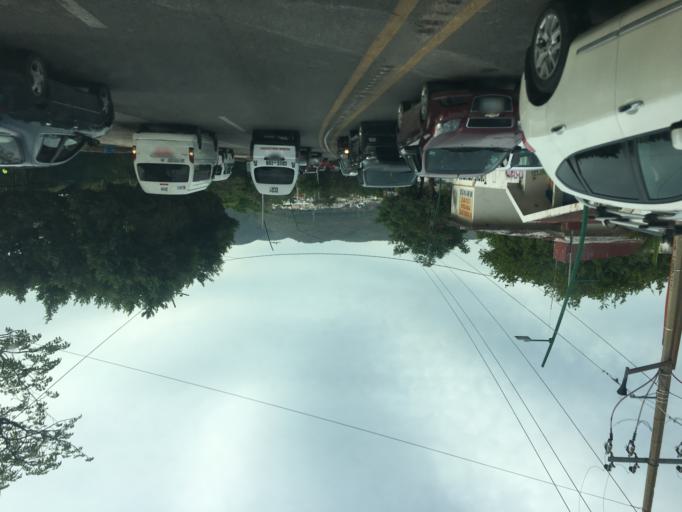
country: MX
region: Chiapas
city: Tuxtla Gutierrez
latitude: 16.7559
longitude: -93.1425
